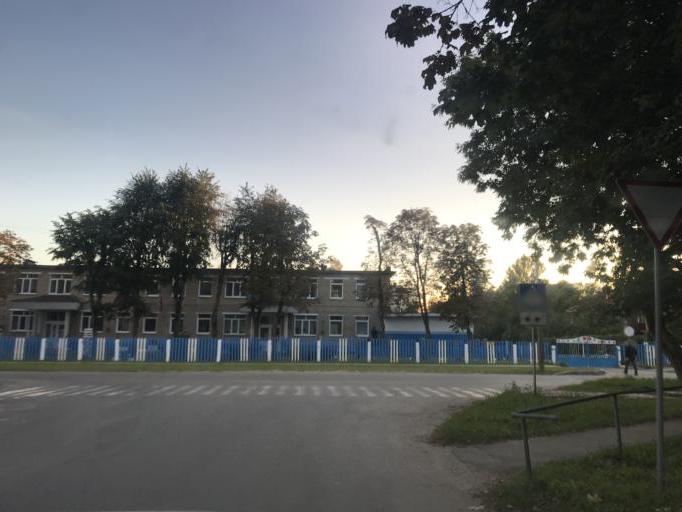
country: BY
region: Mogilev
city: Mahilyow
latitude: 53.9075
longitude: 30.3200
